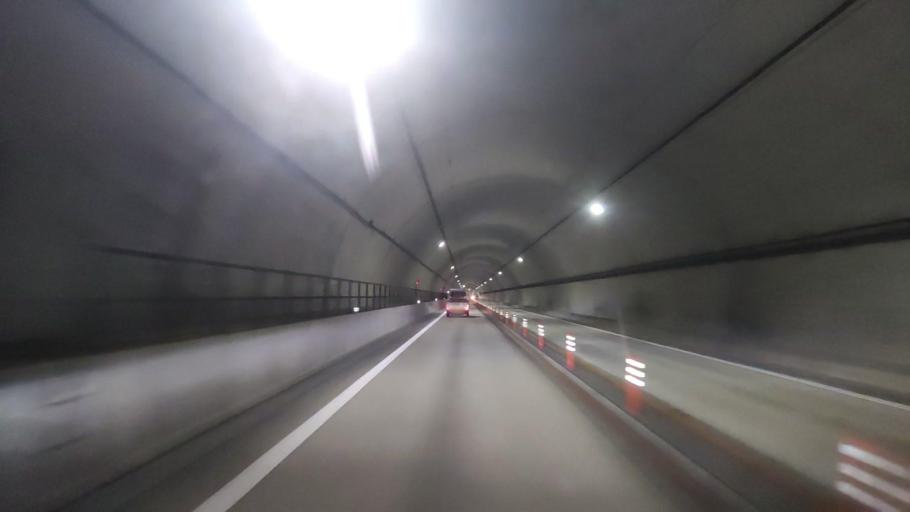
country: JP
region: Wakayama
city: Tanabe
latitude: 33.6018
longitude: 135.4313
